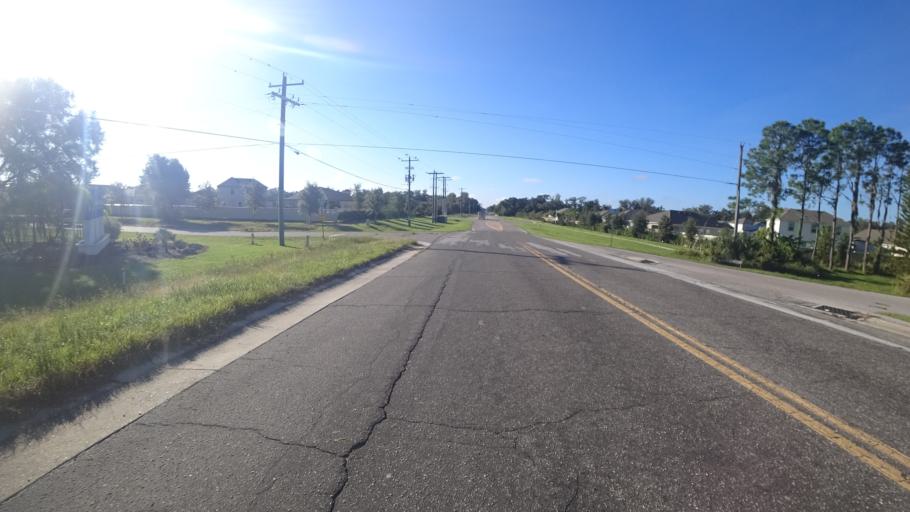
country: US
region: Florida
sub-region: Manatee County
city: Memphis
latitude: 27.5834
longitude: -82.5273
